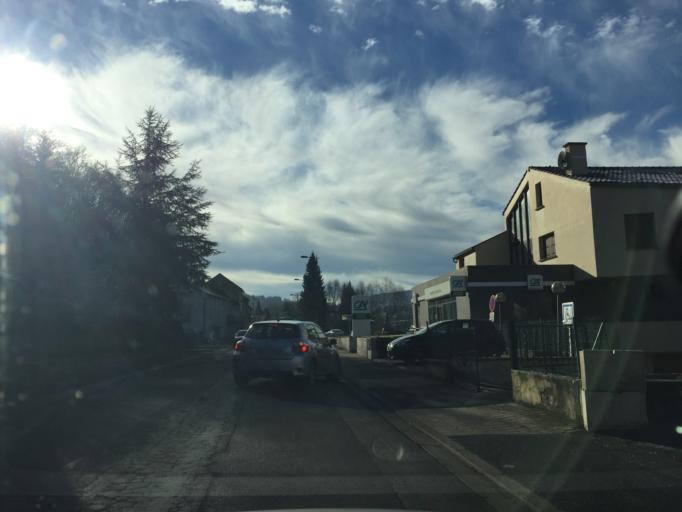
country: FR
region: Auvergne
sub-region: Departement du Puy-de-Dome
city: Gelles
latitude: 45.8667
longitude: 2.6750
